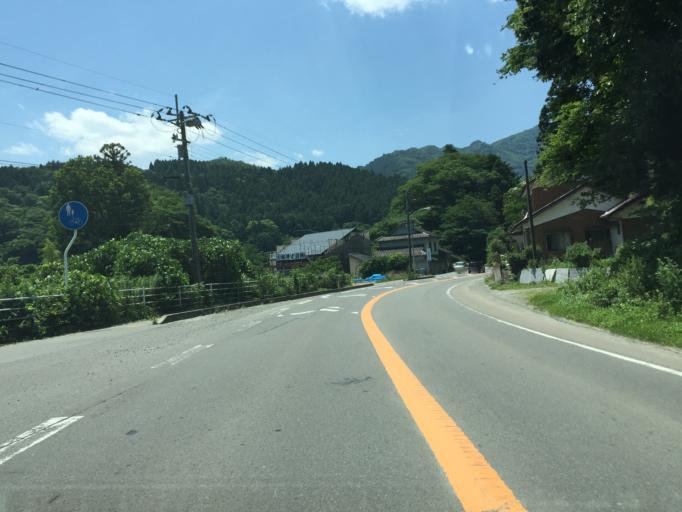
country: JP
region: Miyagi
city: Marumori
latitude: 37.7661
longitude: 140.8596
